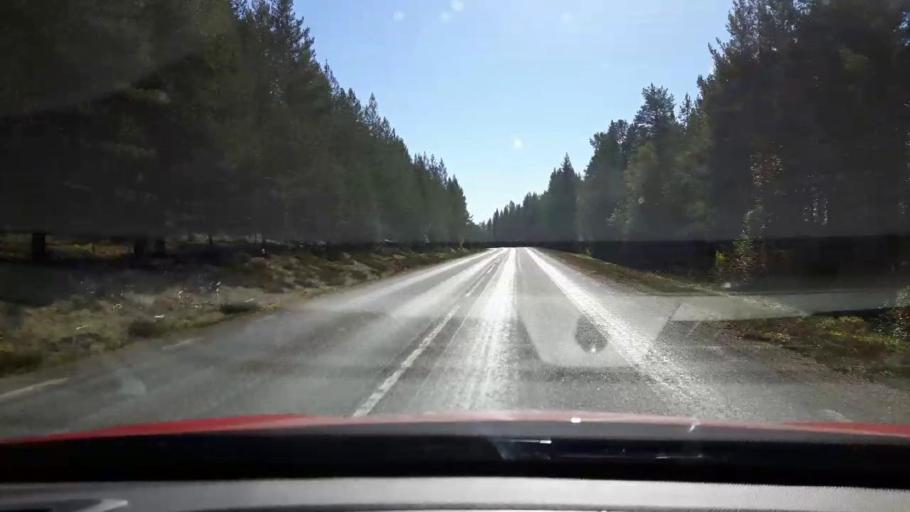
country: SE
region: Jaemtland
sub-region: Harjedalens Kommun
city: Sveg
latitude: 62.3608
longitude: 14.0057
